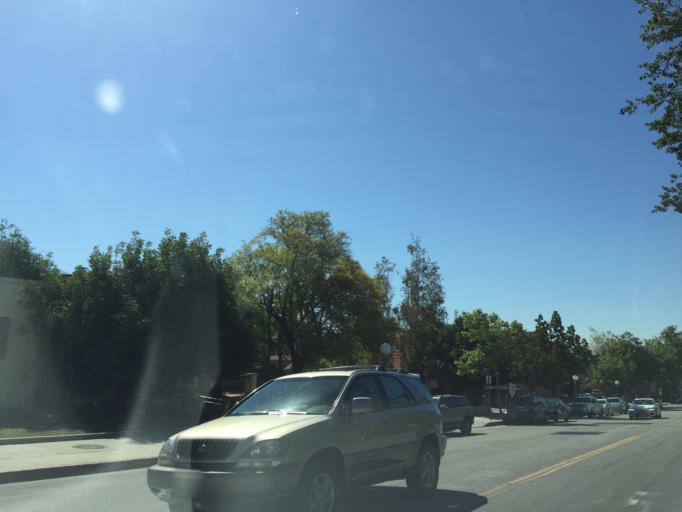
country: US
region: California
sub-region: Los Angeles County
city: Sierra Madre
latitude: 34.1643
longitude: -118.0526
